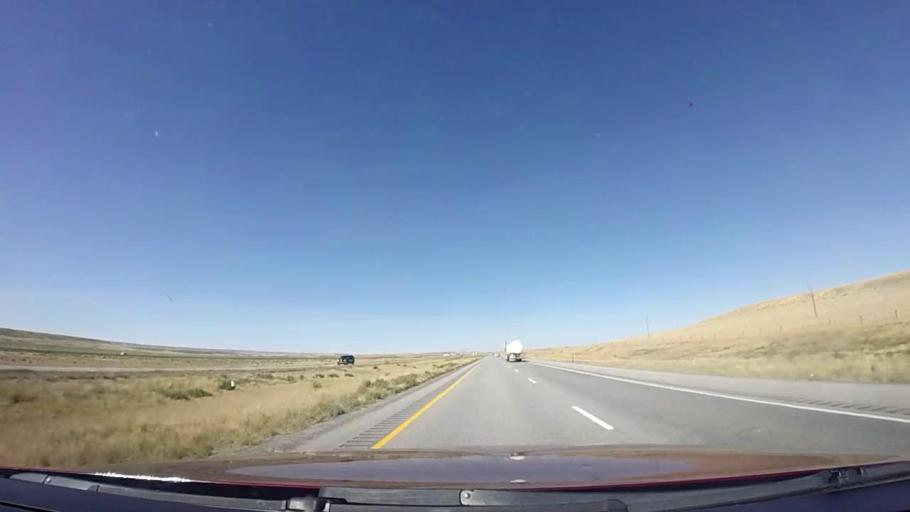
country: US
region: Wyoming
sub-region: Carbon County
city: Rawlins
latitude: 41.6557
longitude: -108.1051
